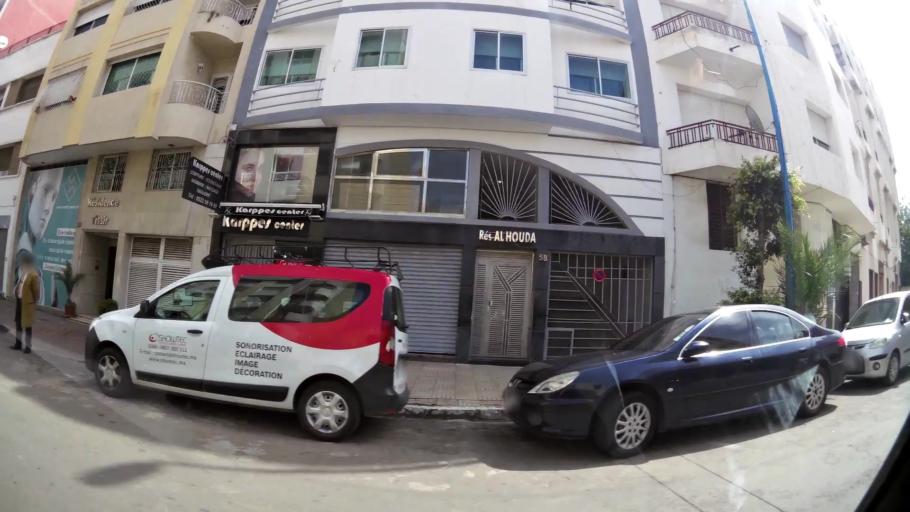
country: MA
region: Grand Casablanca
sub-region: Casablanca
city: Casablanca
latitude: 33.5801
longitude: -7.6427
